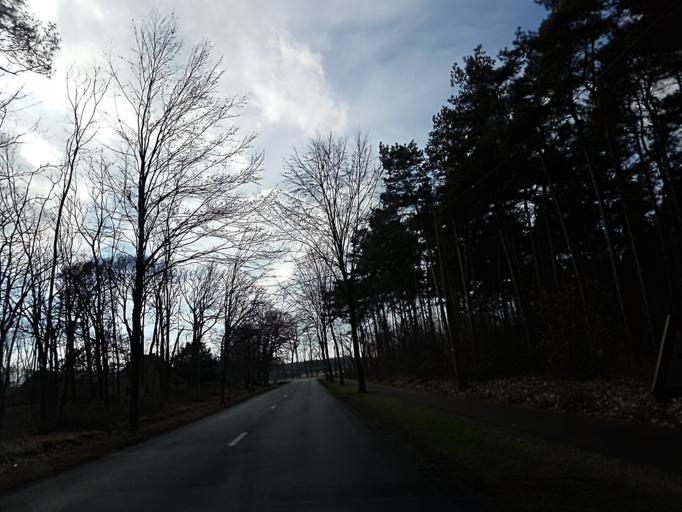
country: BE
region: Flanders
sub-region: Provincie Antwerpen
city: Dessel
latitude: 51.2348
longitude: 5.0927
